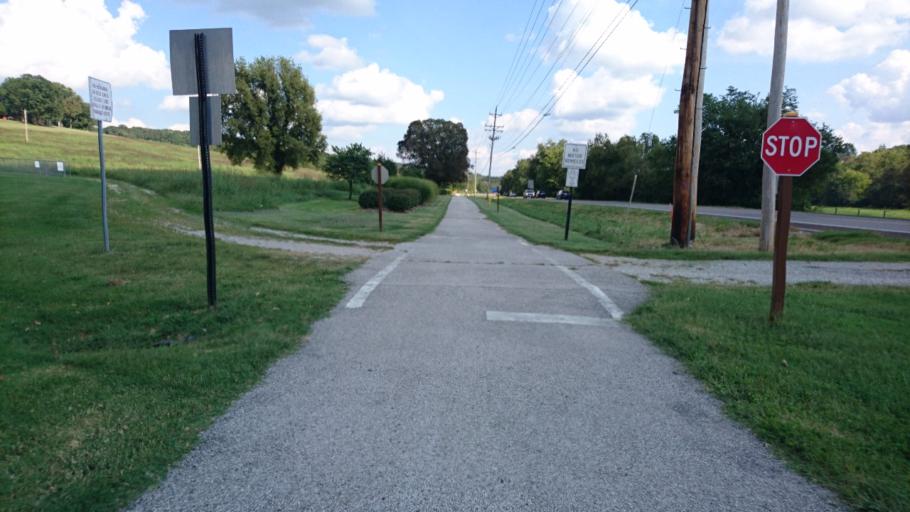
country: US
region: Missouri
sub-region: Saint Louis County
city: Wildwood
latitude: 38.5500
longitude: -90.6368
